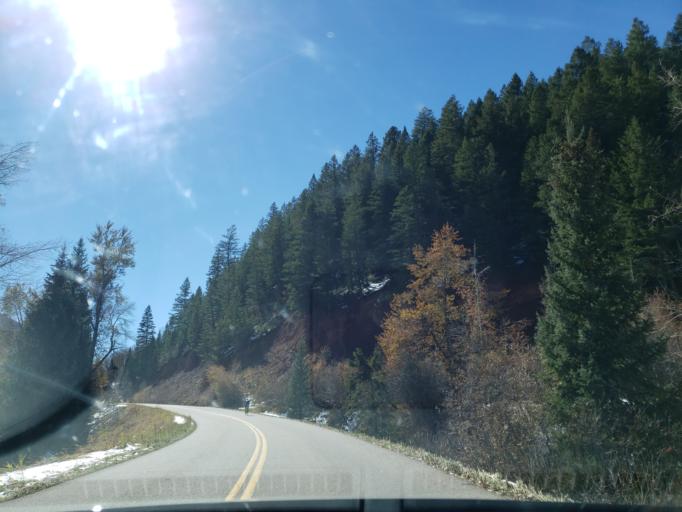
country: US
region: Colorado
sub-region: Pitkin County
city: Snowmass Village
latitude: 39.1351
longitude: -106.9012
